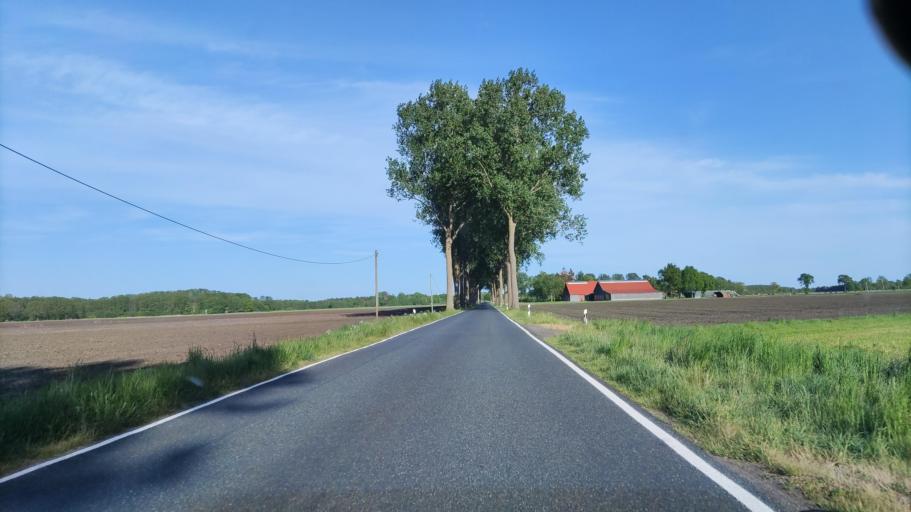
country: DE
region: Lower Saxony
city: Konigsmoor
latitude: 53.2218
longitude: 9.7054
